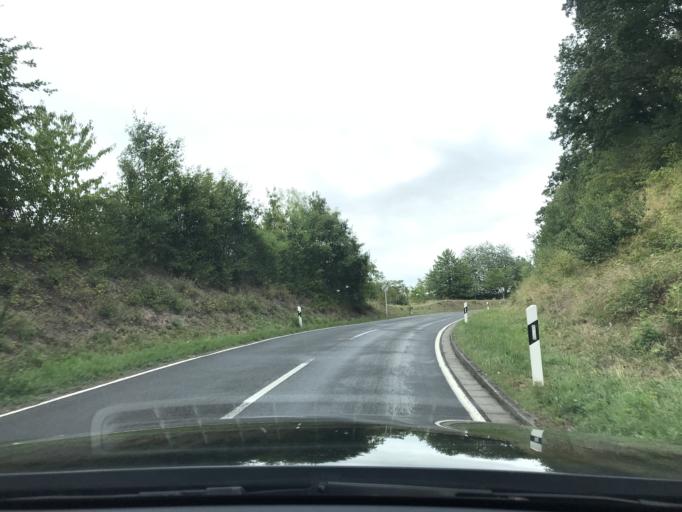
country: DE
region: Bavaria
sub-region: Regierungsbezirk Unterfranken
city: Zeil
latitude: 50.0125
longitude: 10.6094
